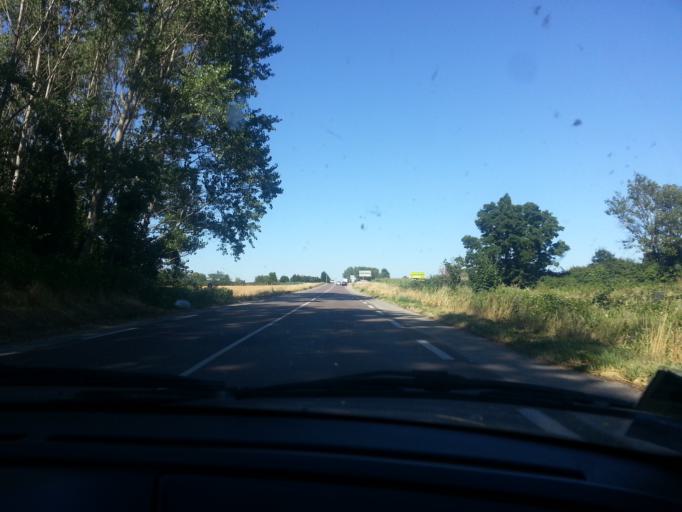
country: FR
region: Bourgogne
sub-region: Departement de Saone-et-Loire
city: Sassenay
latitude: 46.7973
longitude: 4.9303
